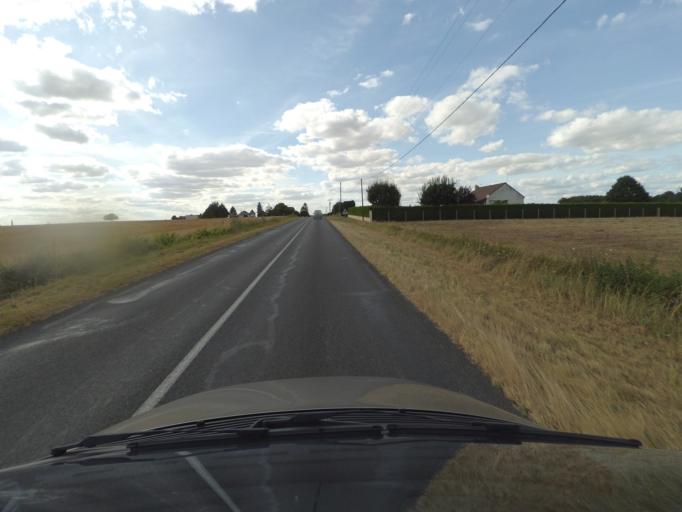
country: FR
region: Centre
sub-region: Departement d'Indre-et-Loire
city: Richelieu
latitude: 46.9887
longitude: 0.3356
